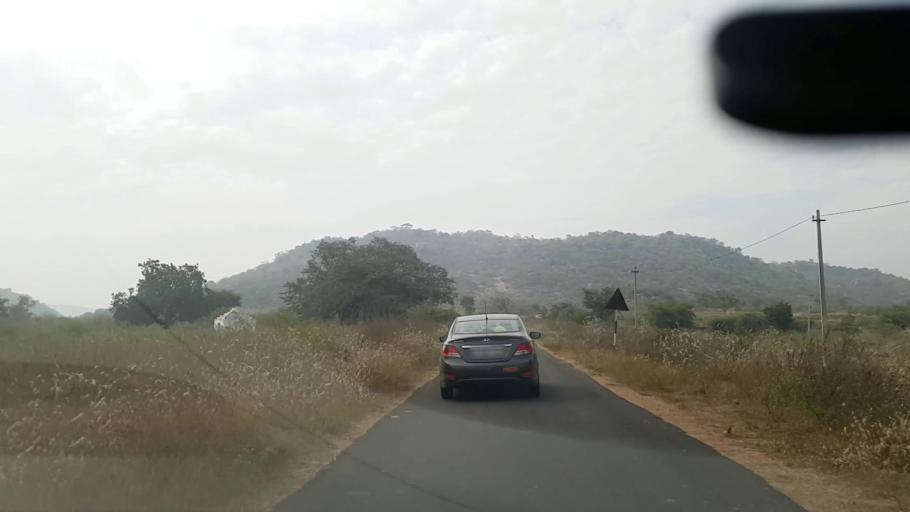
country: IN
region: Telangana
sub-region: Rangareddi
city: Ghatkesar
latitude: 17.1748
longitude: 78.8198
